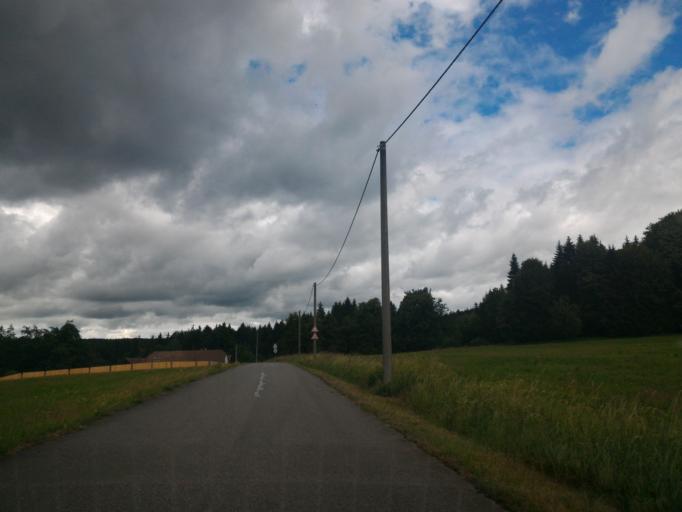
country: CZ
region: Vysocina
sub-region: Okres Jihlava
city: Telc
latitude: 49.2440
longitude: 15.4274
